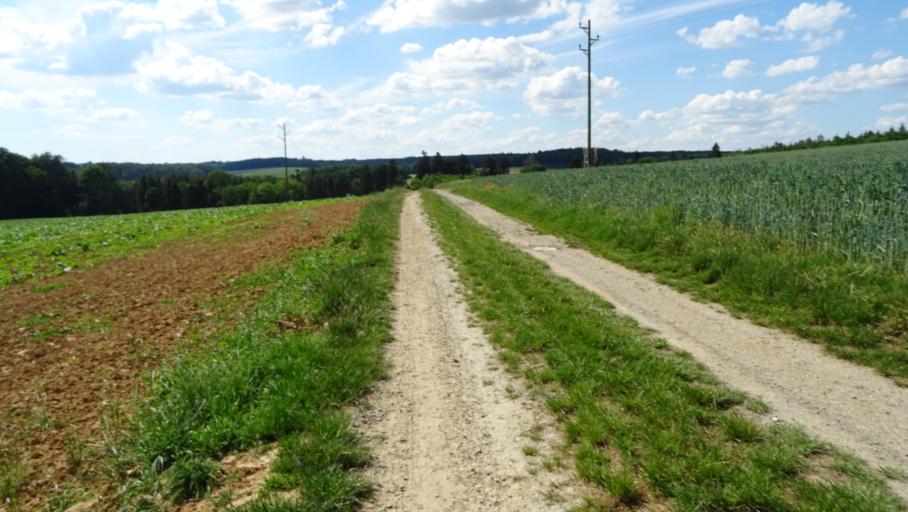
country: DE
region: Baden-Wuerttemberg
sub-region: Karlsruhe Region
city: Adelsheim
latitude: 49.4167
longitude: 9.3661
